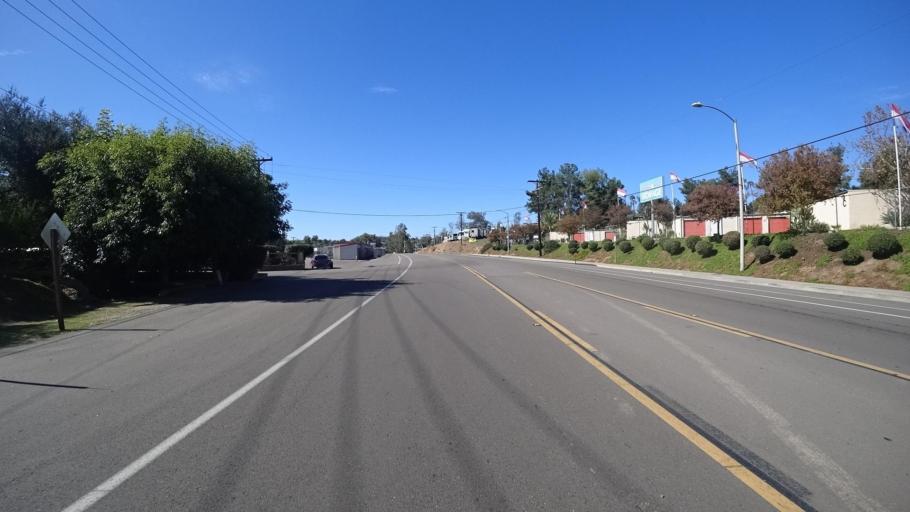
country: US
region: California
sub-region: San Diego County
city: Lakeside
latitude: 32.8401
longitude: -116.8940
